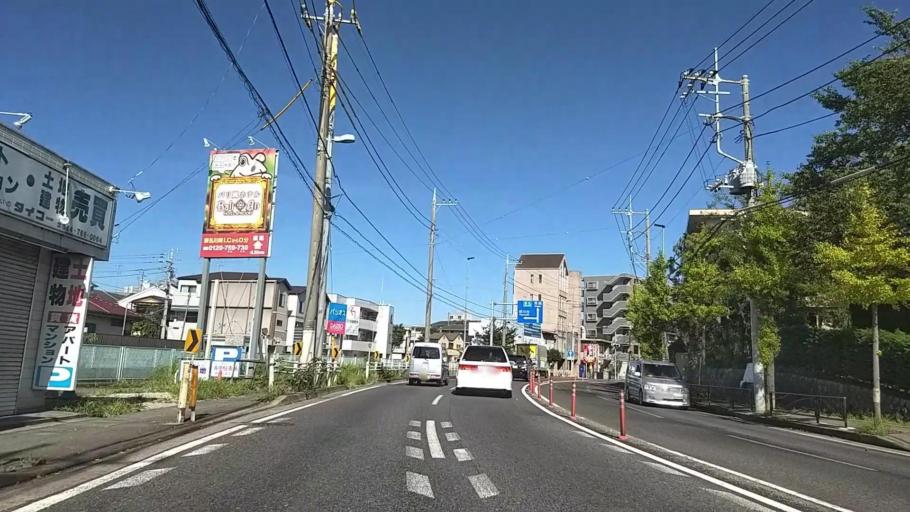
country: JP
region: Tokyo
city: Chofugaoka
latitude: 35.5736
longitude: 139.6130
